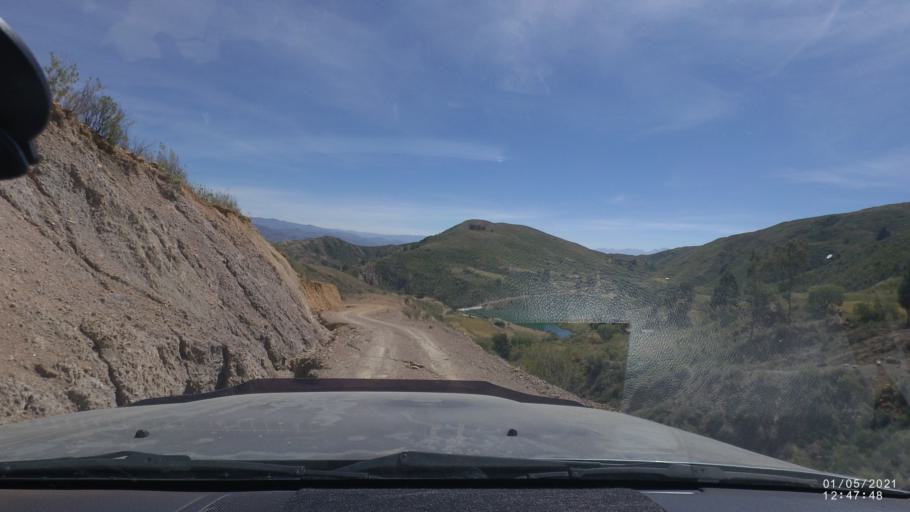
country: BO
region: Cochabamba
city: Capinota
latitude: -17.6868
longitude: -66.1617
